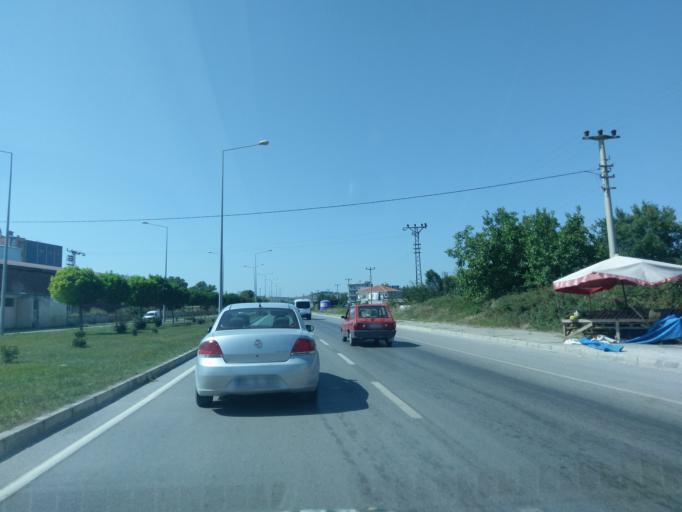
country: TR
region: Samsun
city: Bafra
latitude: 41.5704
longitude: 35.8747
